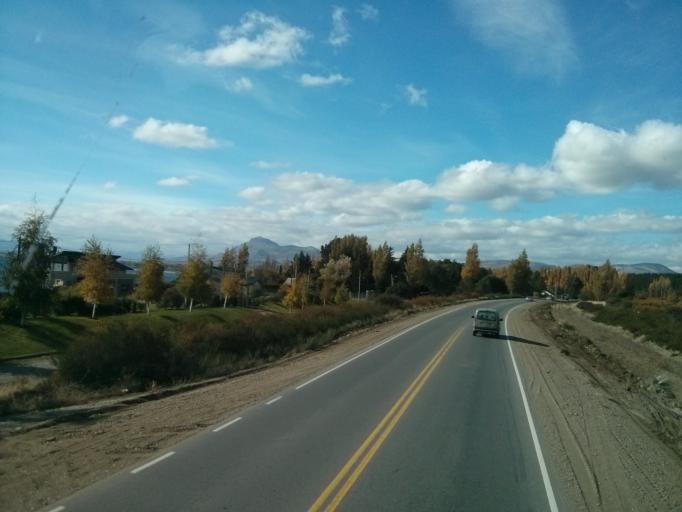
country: AR
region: Rio Negro
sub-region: Departamento de Bariloche
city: San Carlos de Bariloche
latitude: -41.1053
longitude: -71.2034
